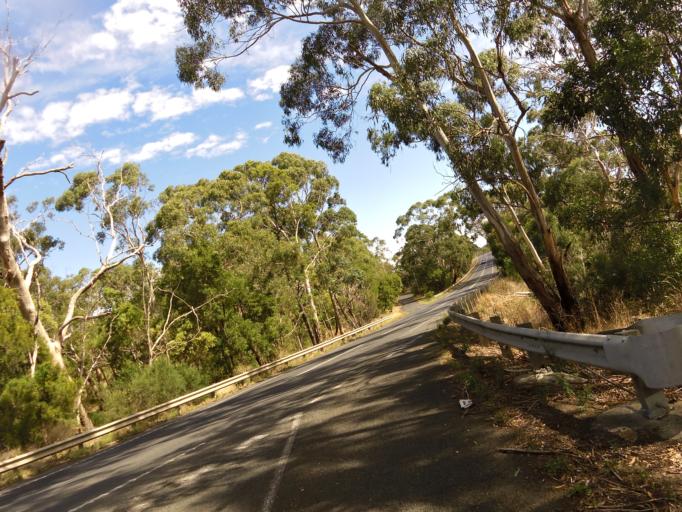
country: AU
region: Victoria
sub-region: Colac-Otway
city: Colac
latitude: -38.3473
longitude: 143.4109
